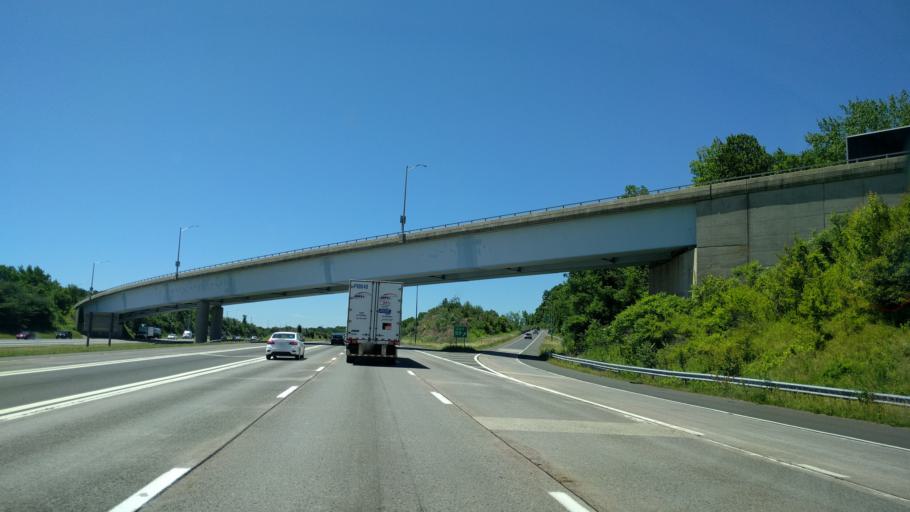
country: US
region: Connecticut
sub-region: Hartford County
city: Manchester
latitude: 41.7876
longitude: -72.5655
